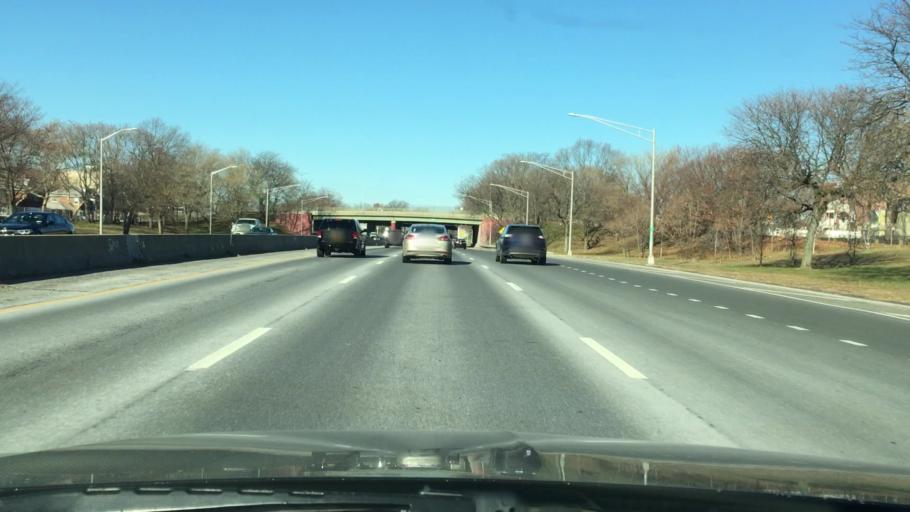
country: US
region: New York
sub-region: Bronx
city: The Bronx
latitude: 40.8330
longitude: -73.8219
